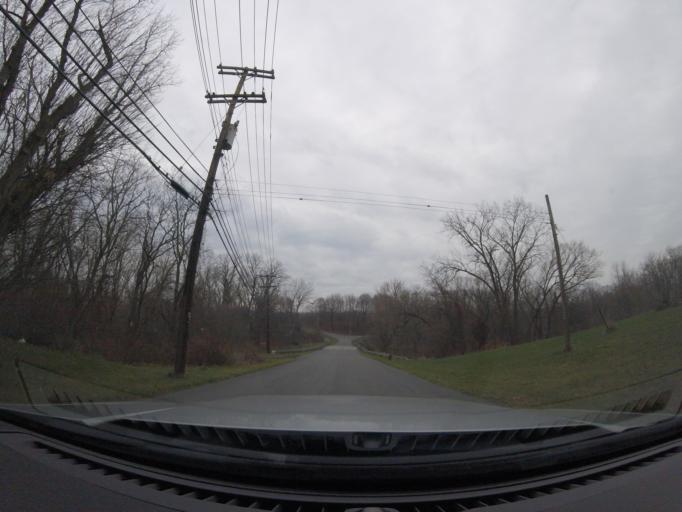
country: US
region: New York
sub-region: Yates County
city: Penn Yan
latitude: 42.6814
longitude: -76.9540
